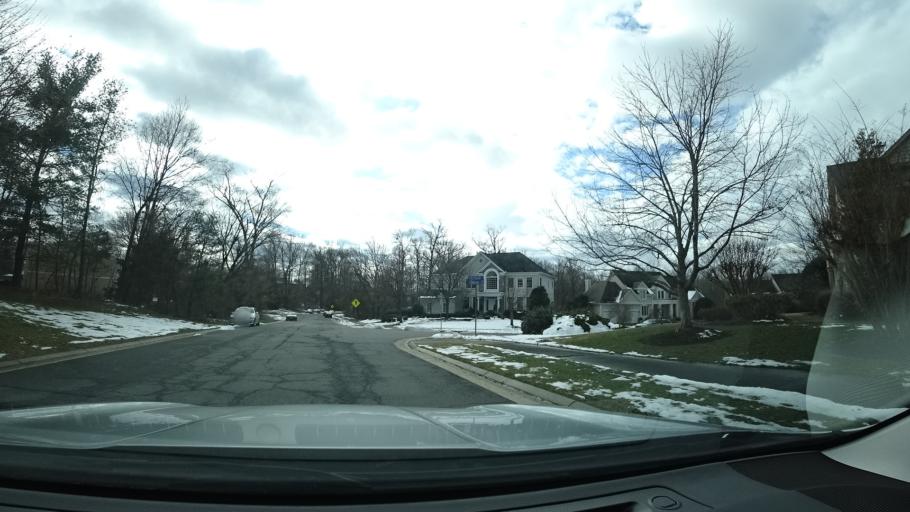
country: US
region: Virginia
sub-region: Fairfax County
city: Herndon
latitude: 38.9747
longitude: -77.3652
